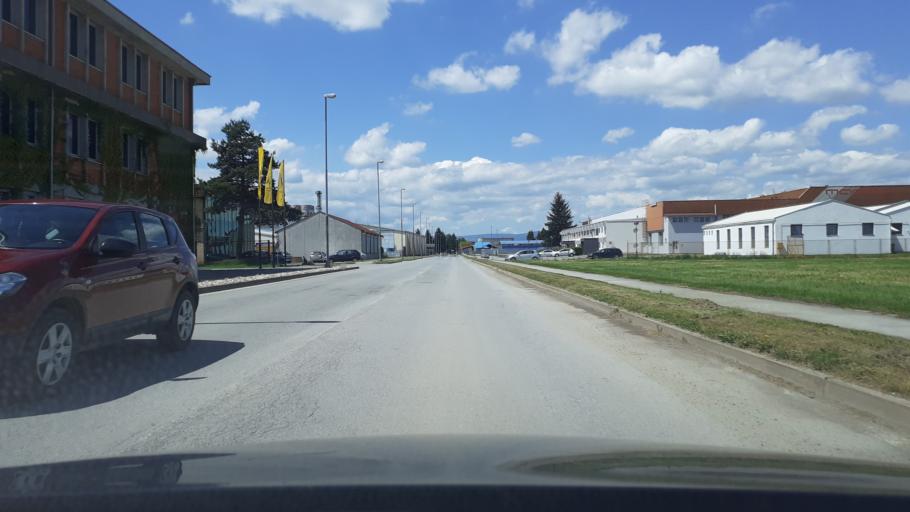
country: HR
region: Pozesko-Slavonska
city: Pozega
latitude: 45.3387
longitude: 17.6965
